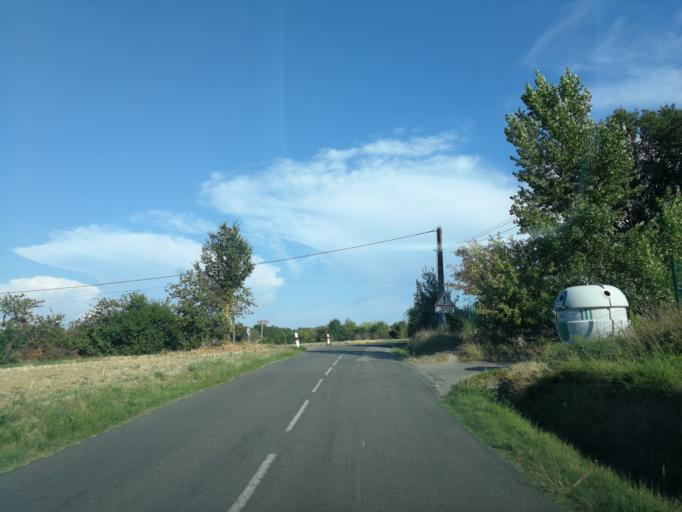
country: FR
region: Midi-Pyrenees
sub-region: Departement de la Haute-Garonne
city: Balma
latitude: 43.6163
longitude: 1.5225
